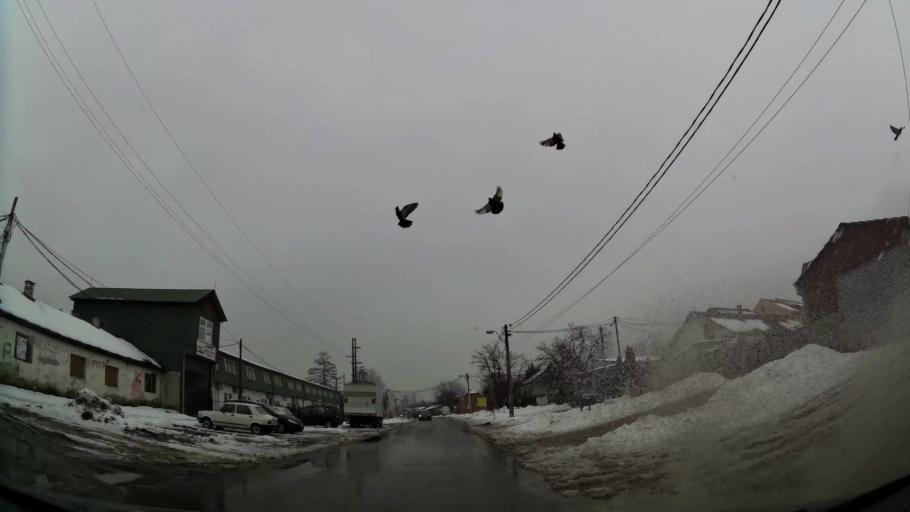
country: RS
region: Central Serbia
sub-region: Belgrade
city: Zemun
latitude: 44.8449
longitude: 20.3755
